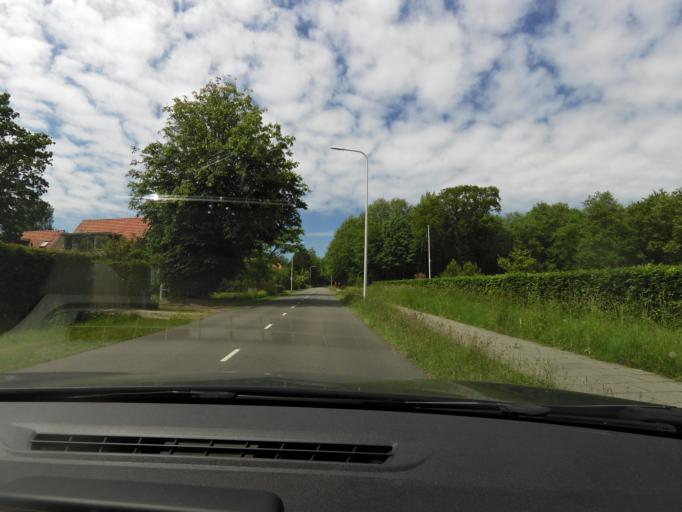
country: NL
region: Zeeland
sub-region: Schouwen-Duiveland
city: Haamstede
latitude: 51.7056
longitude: 3.7361
